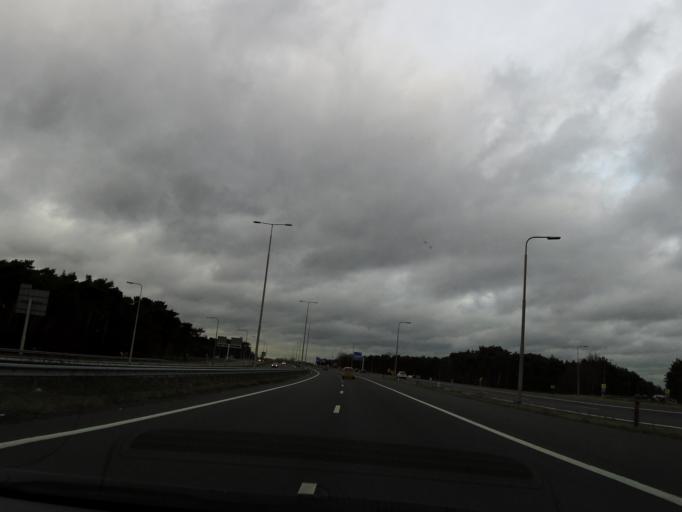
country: NL
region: Limburg
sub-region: Gemeente Venlo
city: Venlo
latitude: 51.3901
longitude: 6.1276
